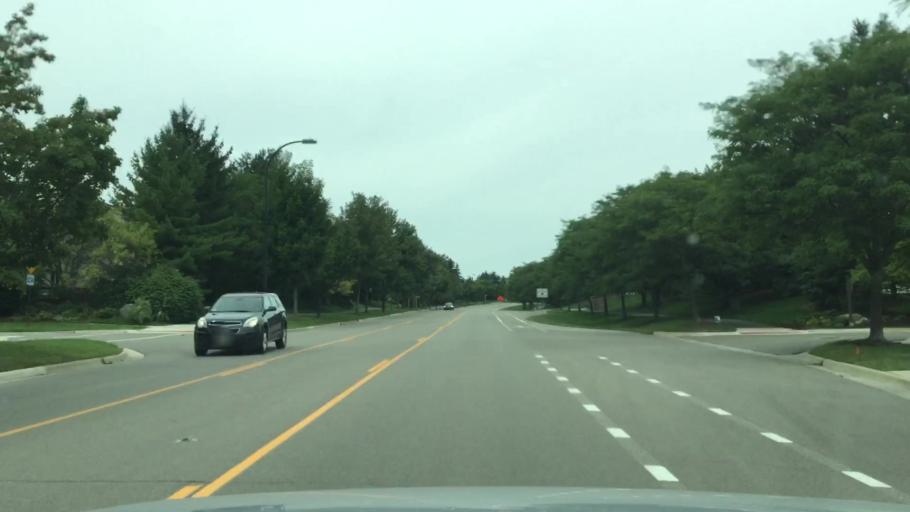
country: US
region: Michigan
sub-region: Washtenaw County
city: Ann Arbor
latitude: 42.3165
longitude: -83.7014
